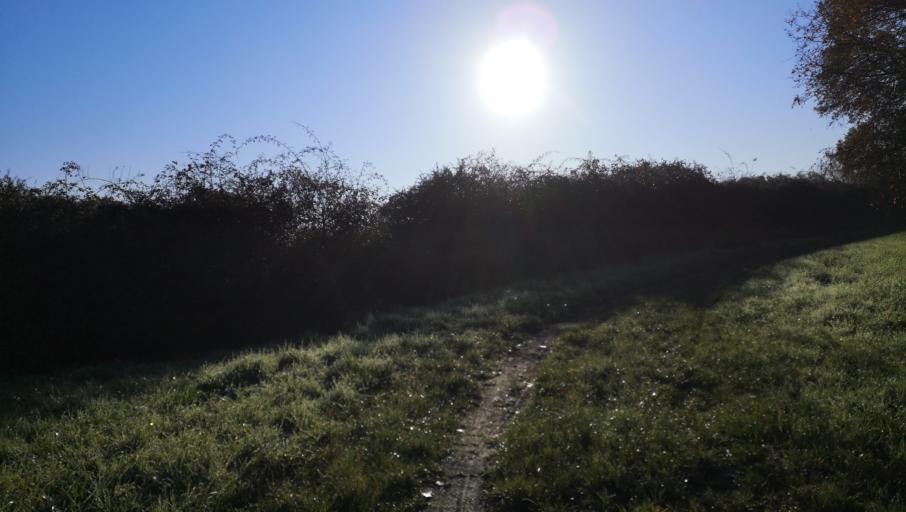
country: FR
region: Centre
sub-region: Departement du Loiret
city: Saran
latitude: 47.9432
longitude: 1.8614
